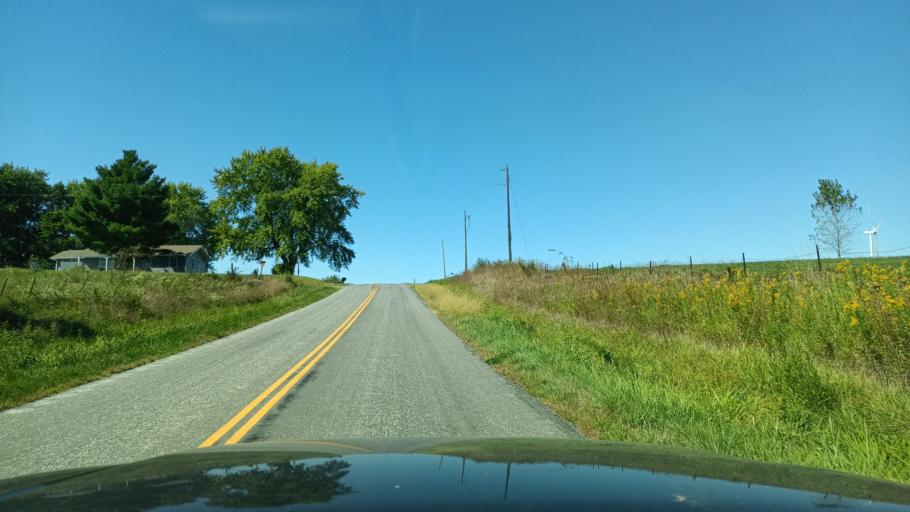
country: US
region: Missouri
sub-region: Adair County
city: Kirksville
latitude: 40.3304
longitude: -92.5228
